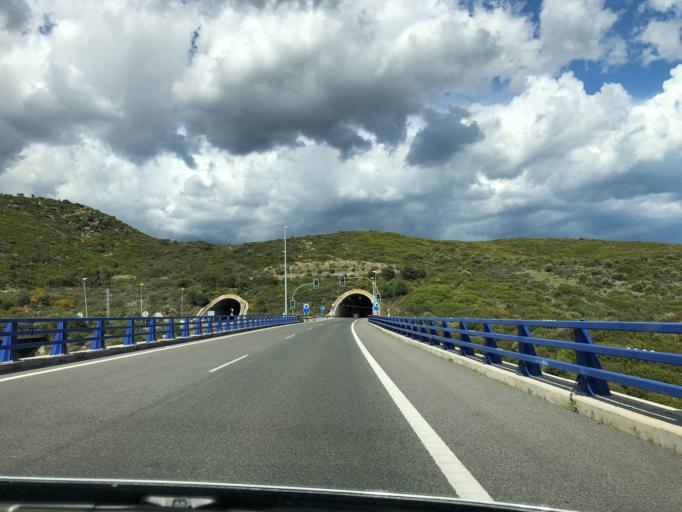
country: ES
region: Andalusia
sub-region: Provincia de Malaga
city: Manilva
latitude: 36.4230
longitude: -5.2149
